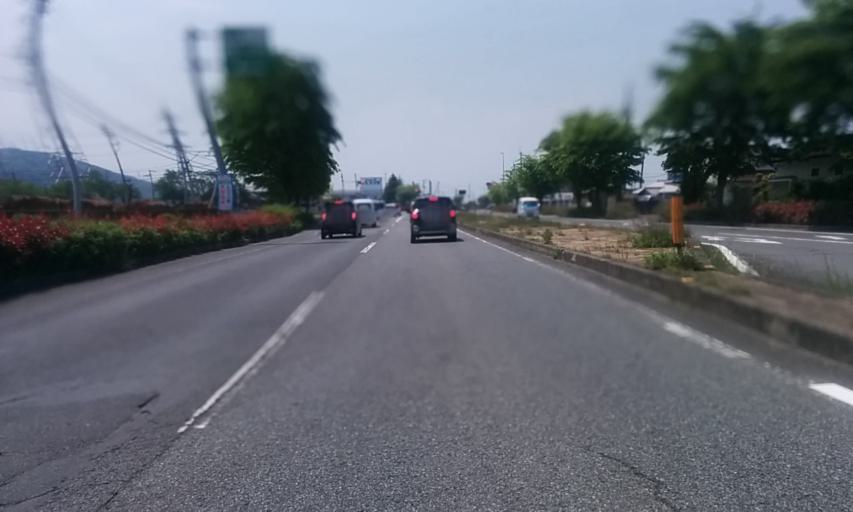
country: JP
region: Ehime
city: Saijo
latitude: 33.9199
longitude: 133.2417
